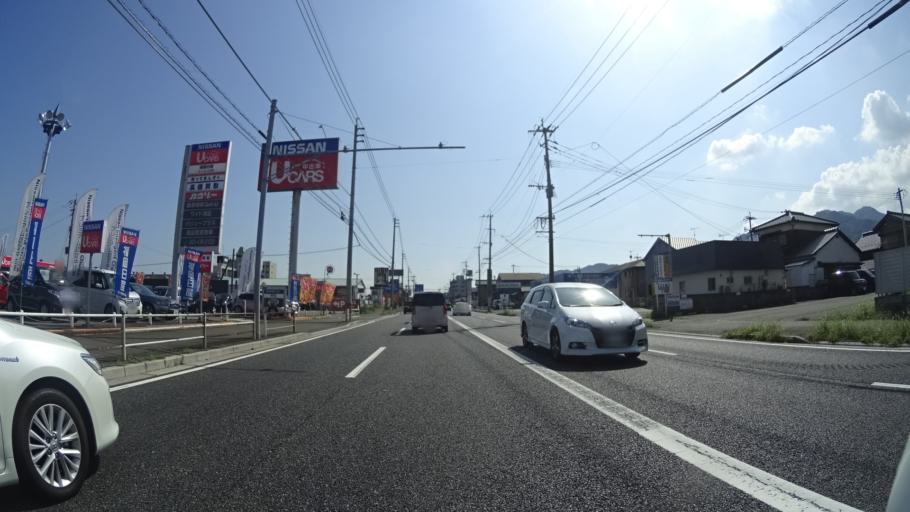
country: JP
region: Fukuoka
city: Kanda
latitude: 33.7712
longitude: 130.9807
